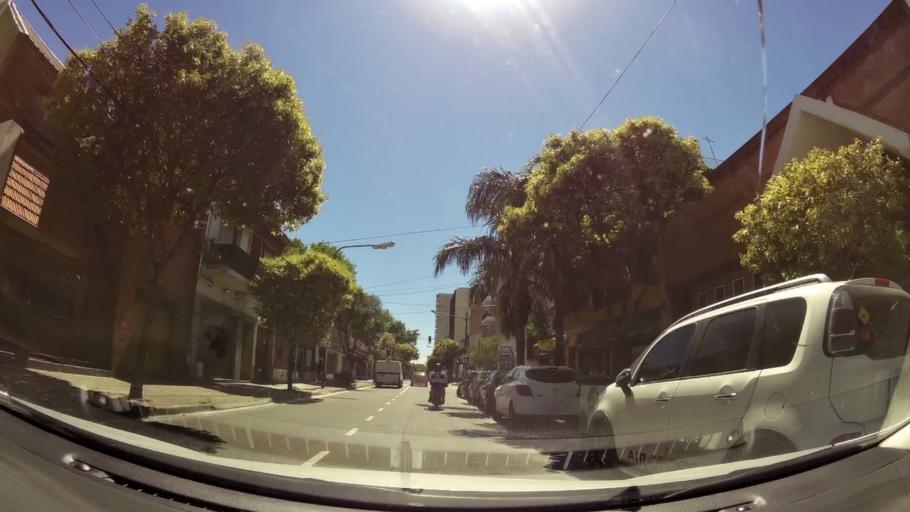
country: AR
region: Buenos Aires
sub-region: Partido de Vicente Lopez
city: Olivos
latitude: -34.5261
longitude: -58.4881
